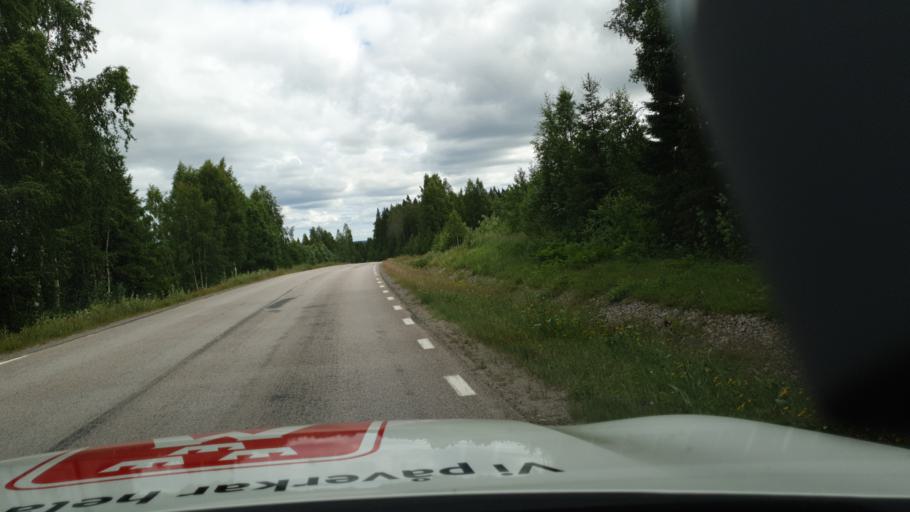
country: SE
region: Vaesterbotten
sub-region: Vannas Kommun
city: Vaennaes
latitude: 63.7927
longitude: 19.8145
